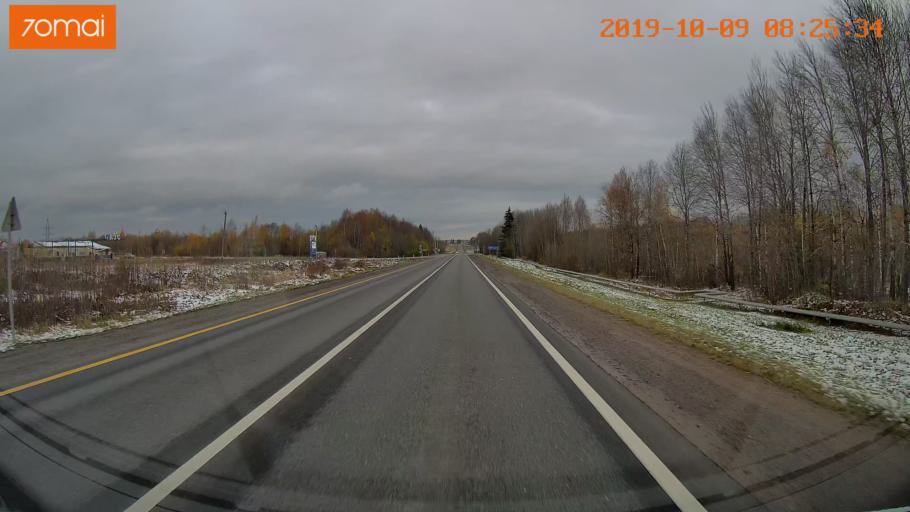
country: RU
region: Vologda
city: Gryazovets
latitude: 58.7830
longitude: 40.2715
